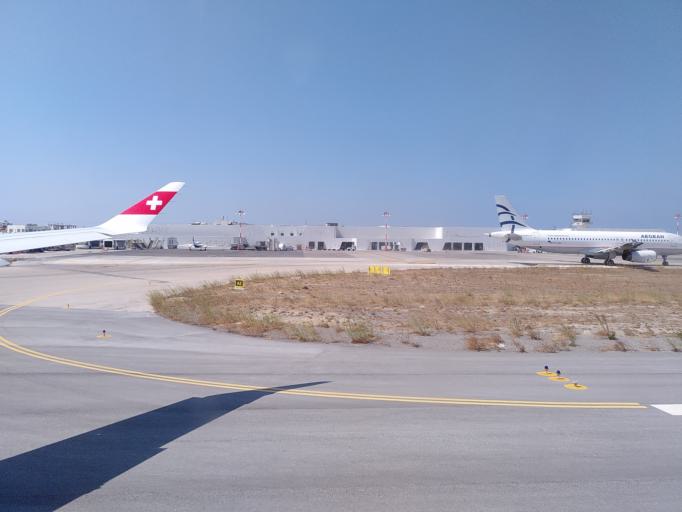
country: GR
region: South Aegean
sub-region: Nomos Kykladon
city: Mykonos
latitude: 37.4346
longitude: 25.3486
